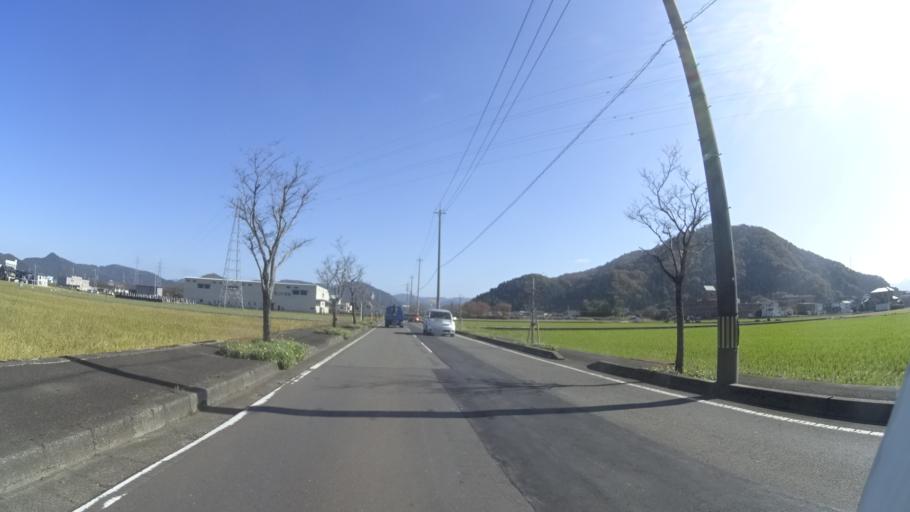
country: JP
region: Fukui
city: Sabae
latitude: 35.9496
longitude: 136.2036
